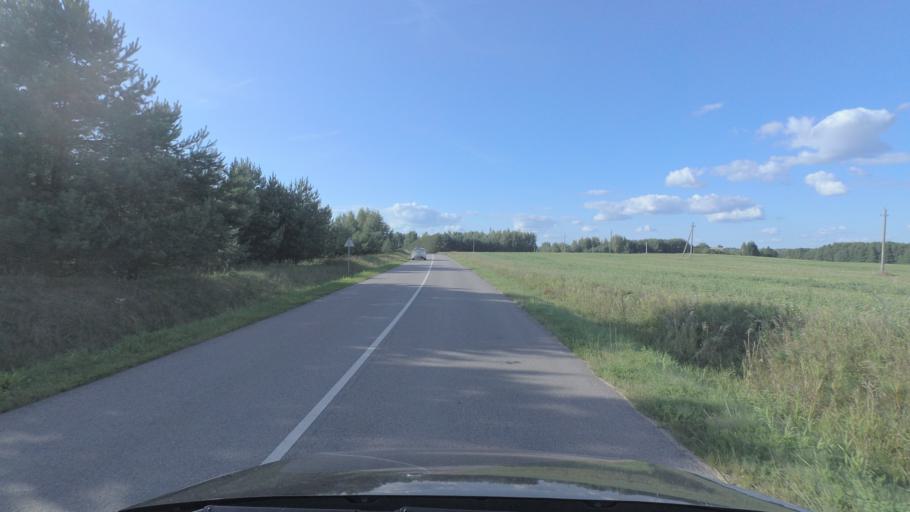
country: LT
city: Pabrade
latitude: 55.0914
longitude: 25.6859
